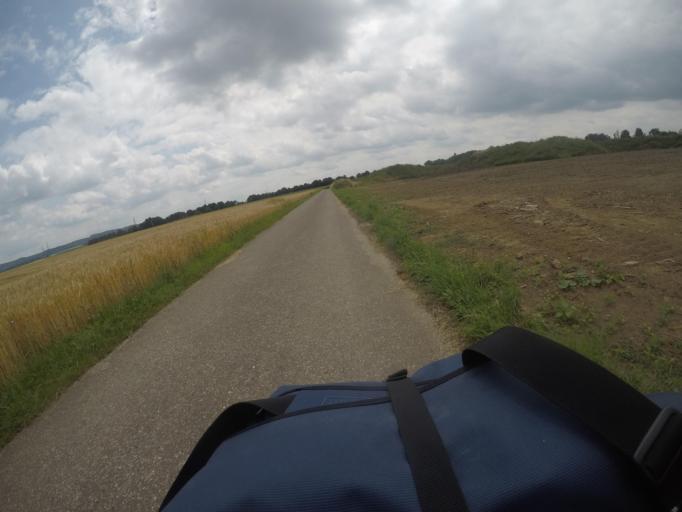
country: DE
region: Bavaria
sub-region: Swabia
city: Heimertingen
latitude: 48.0505
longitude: 10.1568
